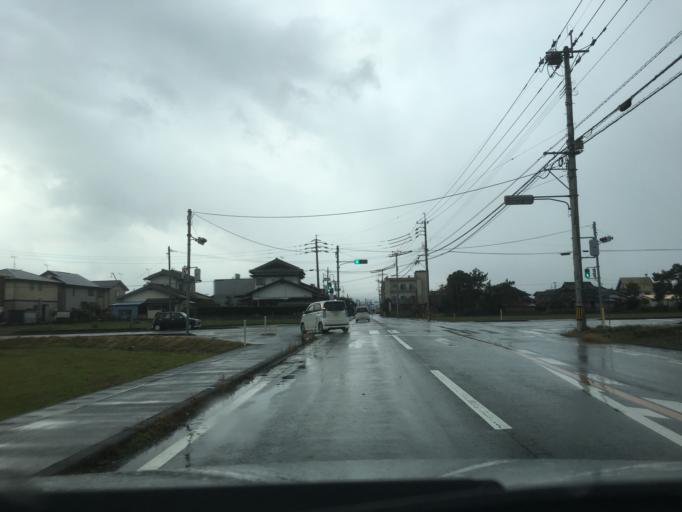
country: JP
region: Saga Prefecture
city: Tosu
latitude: 33.3778
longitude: 130.5643
